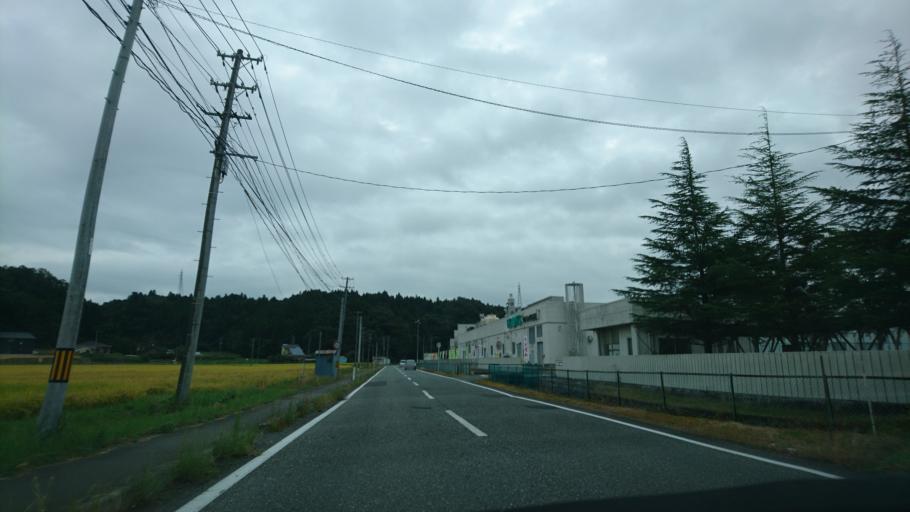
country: JP
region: Iwate
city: Ichinoseki
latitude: 38.8103
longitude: 141.0801
